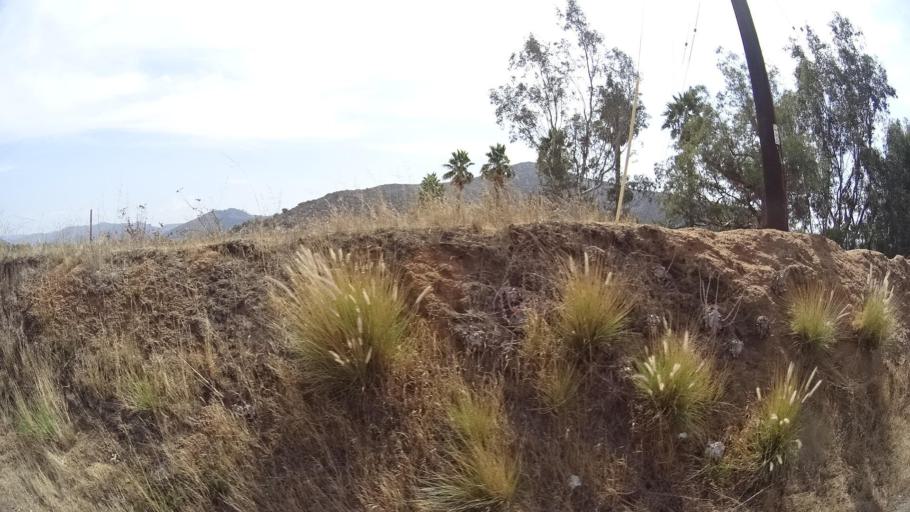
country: US
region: California
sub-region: San Diego County
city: San Pasqual
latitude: 33.0866
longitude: -117.0238
